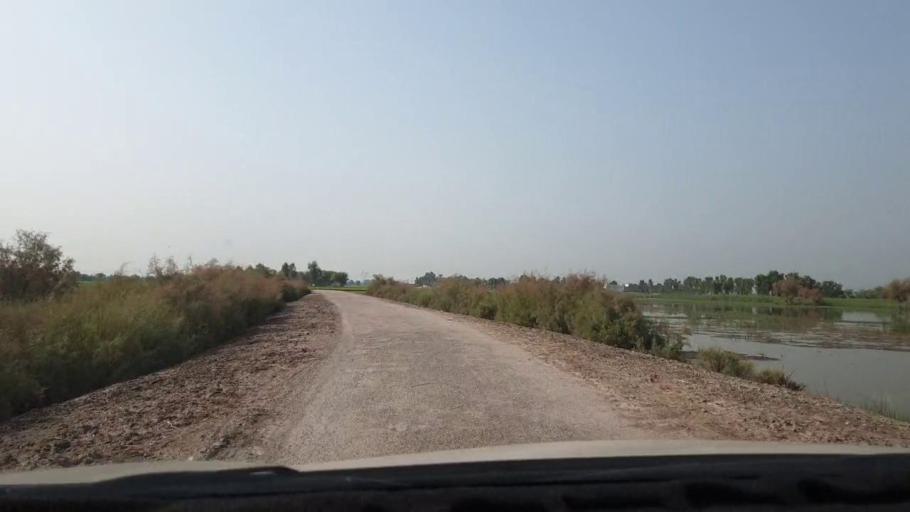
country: PK
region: Sindh
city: Goth Garelo
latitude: 27.4925
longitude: 68.1138
